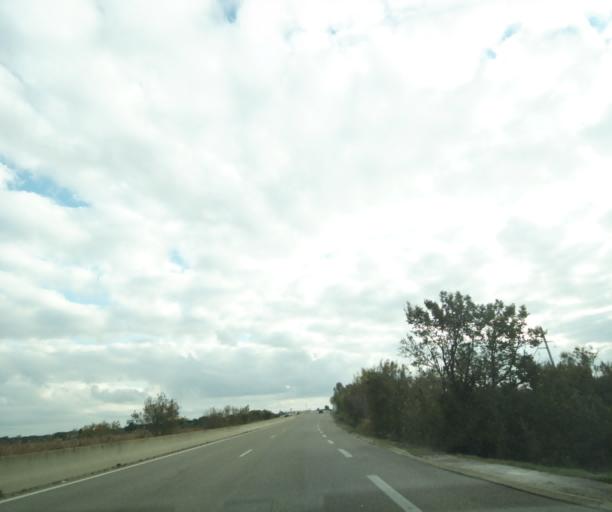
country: FR
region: Languedoc-Roussillon
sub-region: Departement du Gard
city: Aigues-Mortes
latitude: 43.5925
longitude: 4.1960
